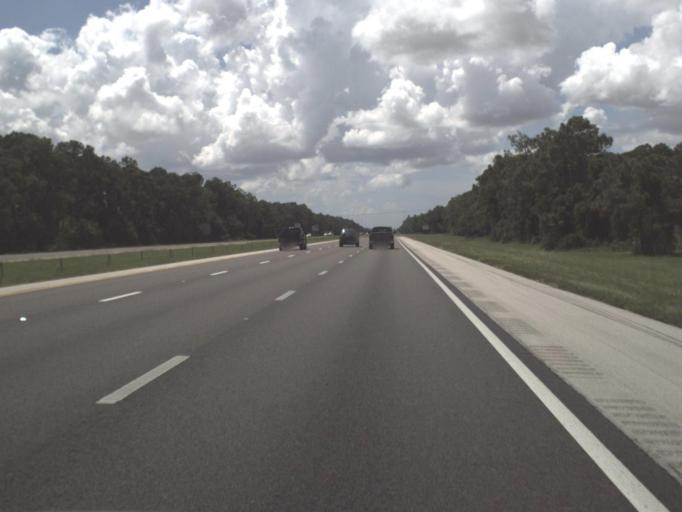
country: US
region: Florida
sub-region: Collier County
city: Vineyards
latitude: 26.2349
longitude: -81.7368
